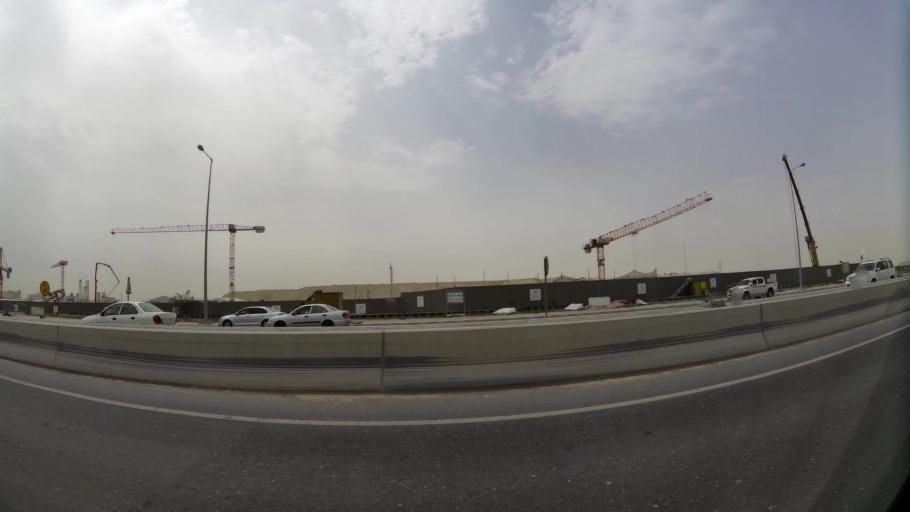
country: QA
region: Baladiyat ad Dawhah
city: Doha
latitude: 25.2945
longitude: 51.4836
